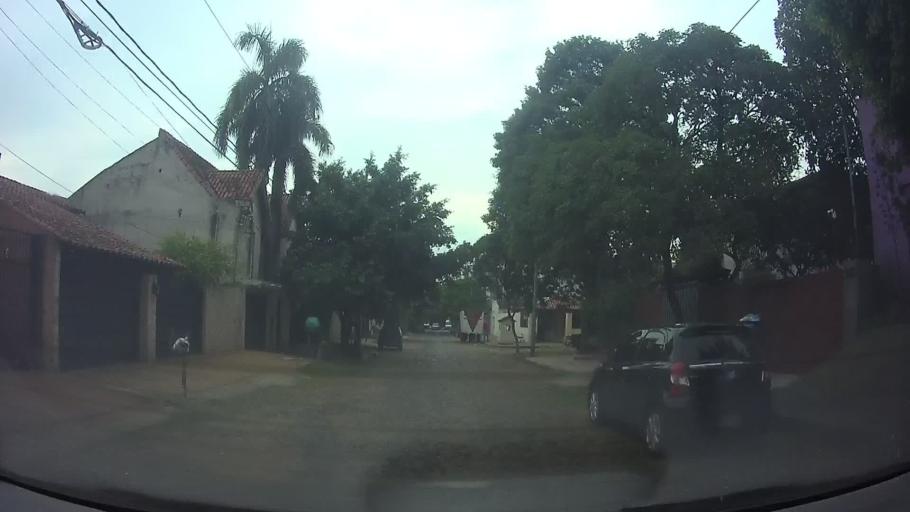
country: PY
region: Asuncion
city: Asuncion
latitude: -25.2801
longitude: -57.5726
